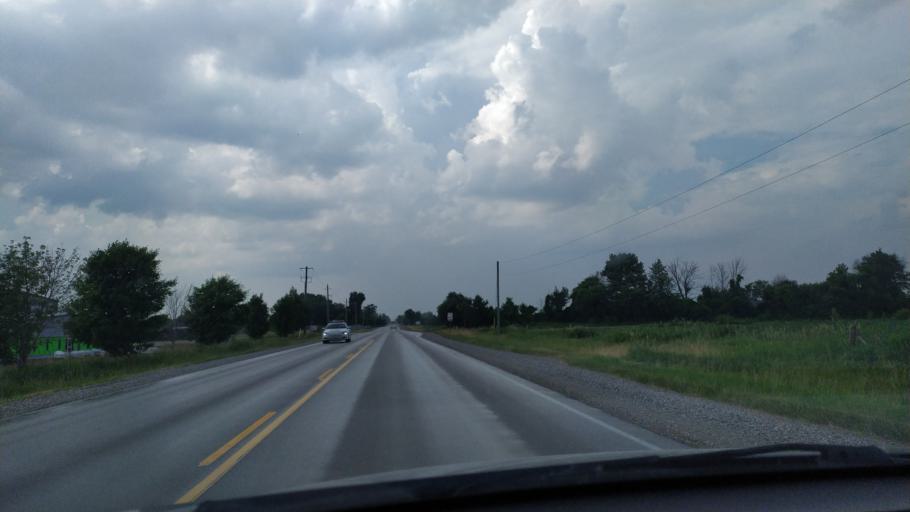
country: CA
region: Ontario
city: London
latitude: 43.0937
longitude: -81.1526
